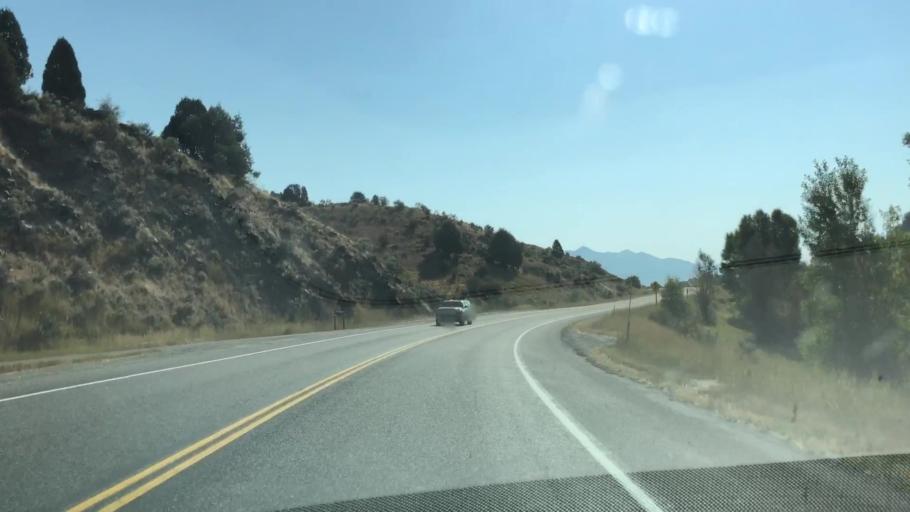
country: US
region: Idaho
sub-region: Teton County
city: Victor
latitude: 43.4511
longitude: -111.3950
